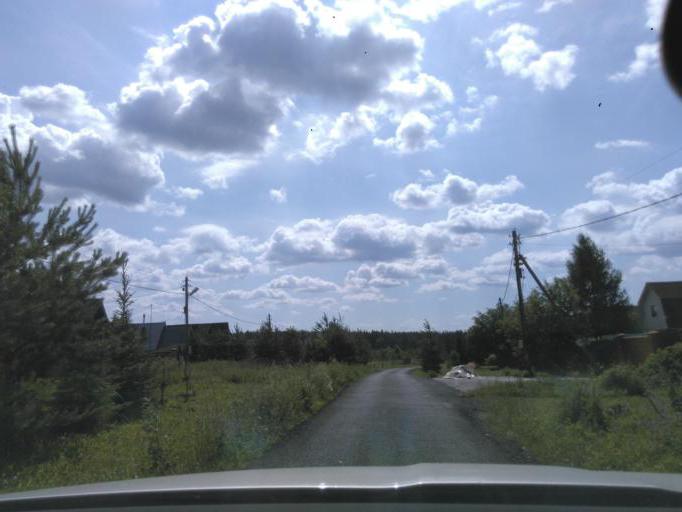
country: RU
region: Moskovskaya
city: Solnechnogorsk
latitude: 56.1298
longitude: 36.9659
